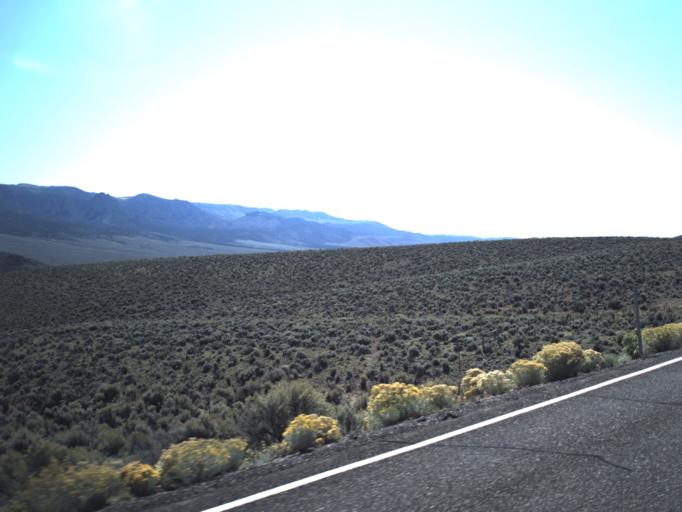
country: US
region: Utah
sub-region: Piute County
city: Junction
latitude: 38.3240
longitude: -111.9619
